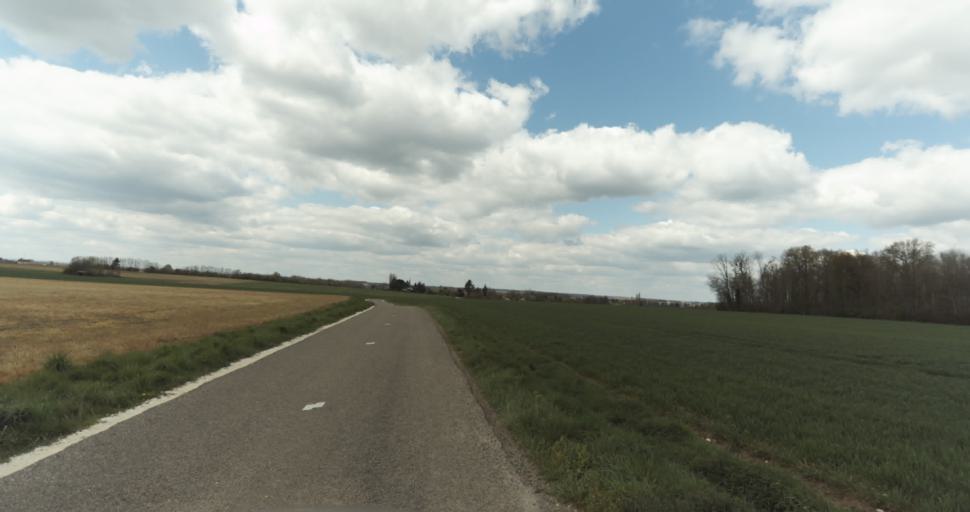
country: FR
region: Bourgogne
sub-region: Departement de la Cote-d'Or
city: Auxonne
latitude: 47.1825
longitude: 5.4129
